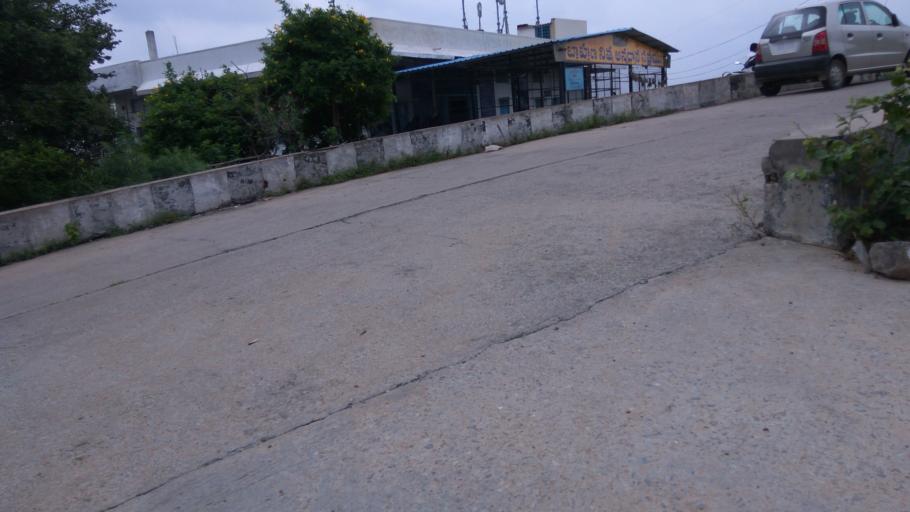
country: IN
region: Telangana
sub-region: Rangareddi
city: Ghatkesar
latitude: 17.5284
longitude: 78.6887
